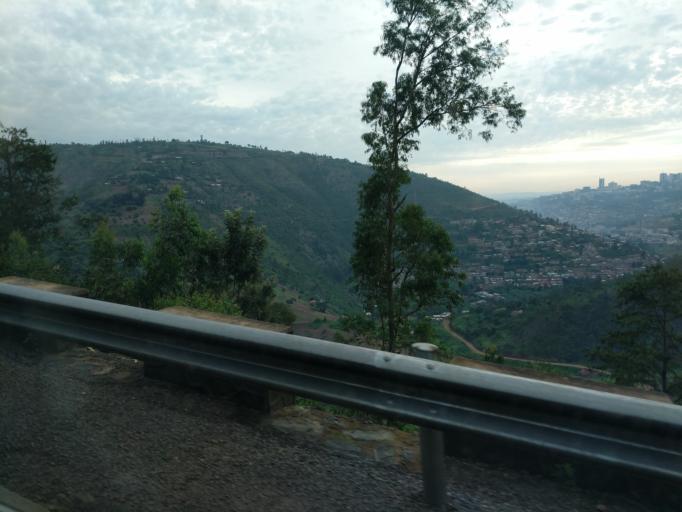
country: RW
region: Kigali
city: Kigali
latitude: -1.9393
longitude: 30.0281
